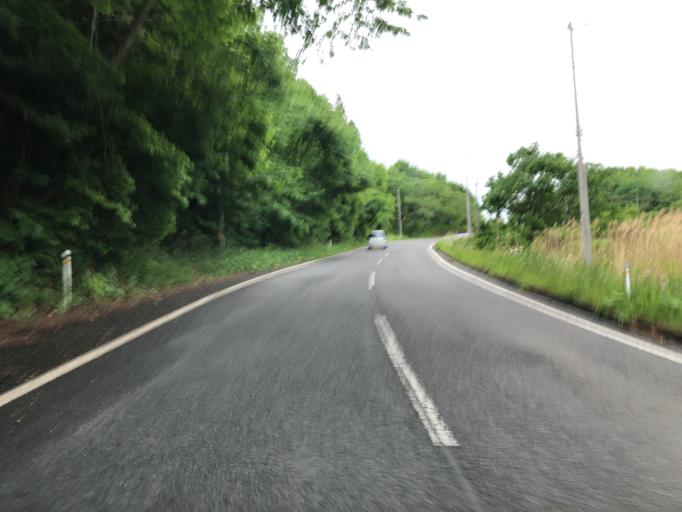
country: JP
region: Fukushima
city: Miharu
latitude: 37.4732
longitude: 140.4757
